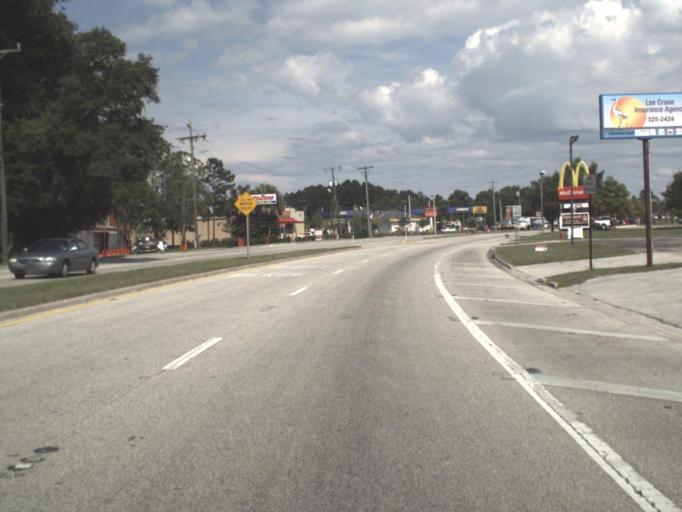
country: US
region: Florida
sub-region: Putnam County
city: Palatka
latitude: 29.6561
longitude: -81.6592
